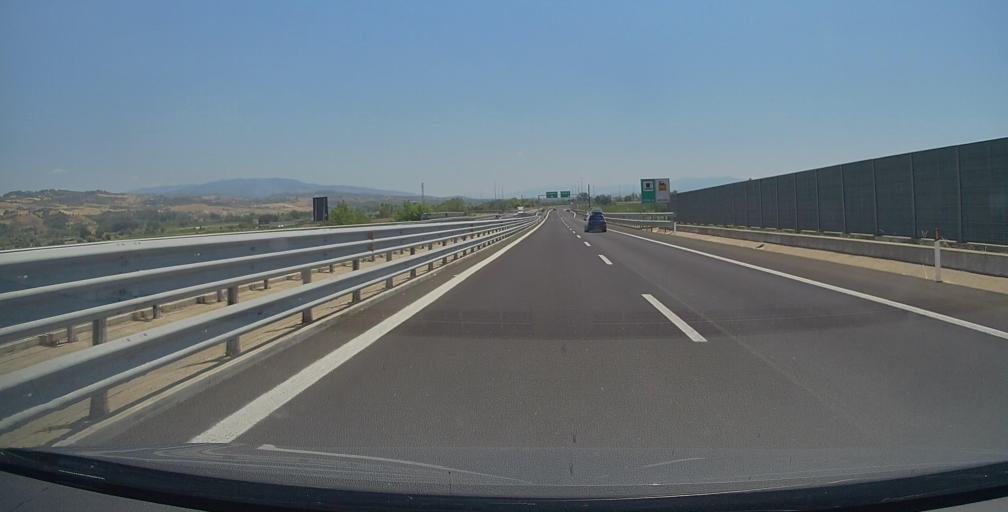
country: IT
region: Calabria
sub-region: Provincia di Cosenza
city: Tarsia
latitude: 39.5891
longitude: 16.2459
